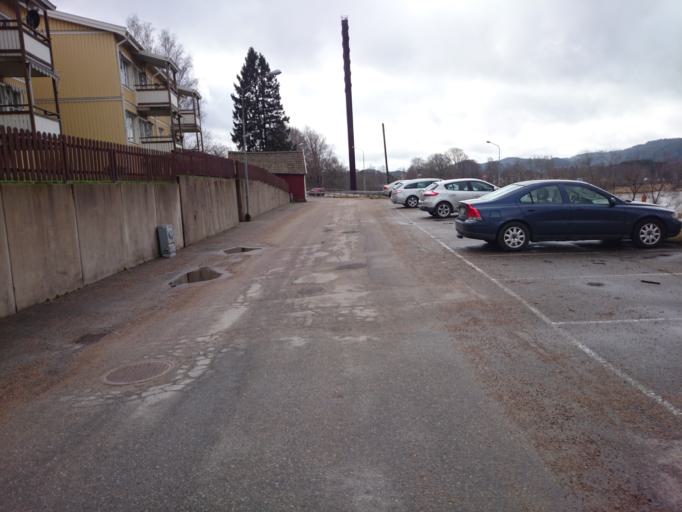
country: SE
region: Vaestra Goetaland
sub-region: Lilla Edets Kommun
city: Lilla Edet
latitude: 58.1345
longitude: 12.1223
